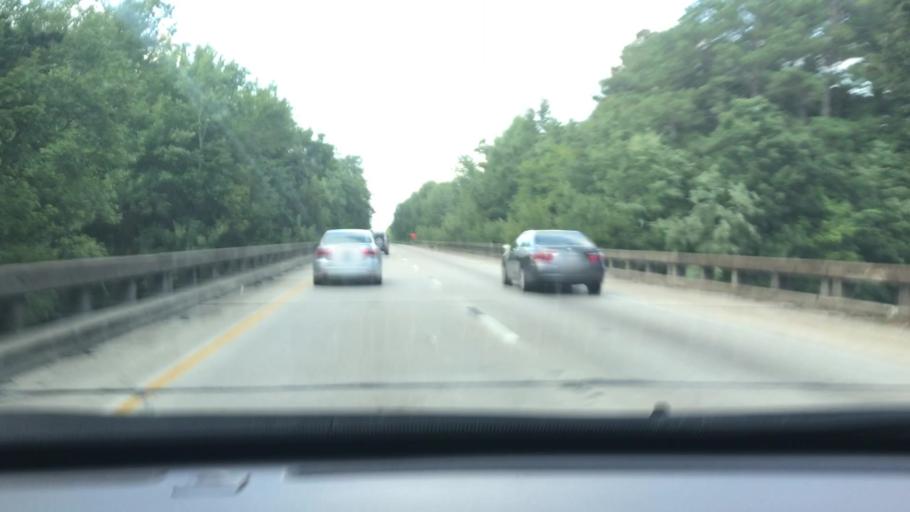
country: US
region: South Carolina
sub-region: Florence County
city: Timmonsville
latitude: 34.0375
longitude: -79.9858
